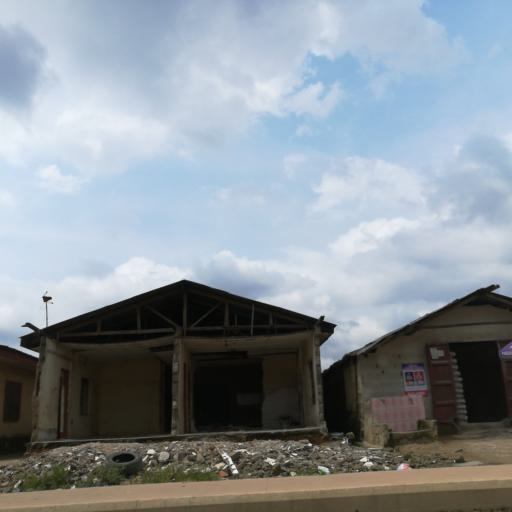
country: NG
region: Rivers
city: Port Harcourt
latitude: 4.8487
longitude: 7.0640
